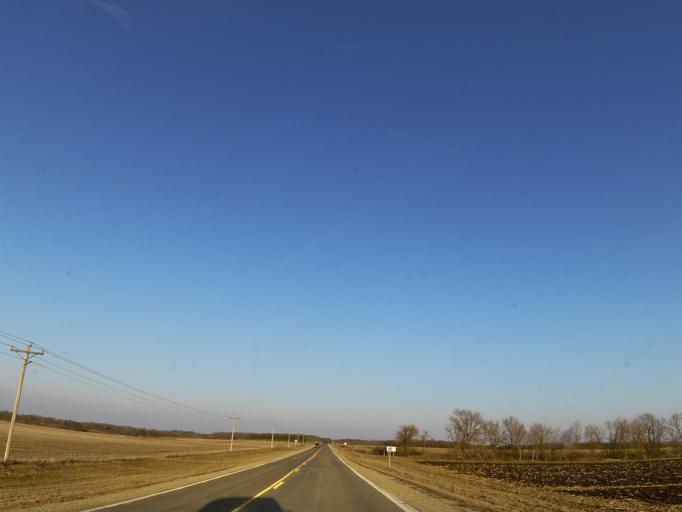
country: US
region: Iowa
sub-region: Mitchell County
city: Saint Ansgar
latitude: 43.3933
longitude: -92.9571
